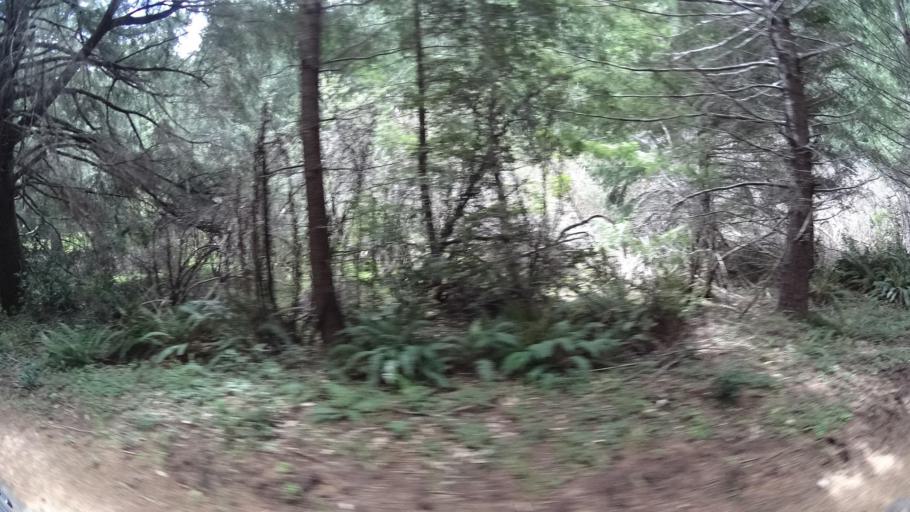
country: US
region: California
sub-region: Humboldt County
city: Redway
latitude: 40.0176
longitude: -124.0005
